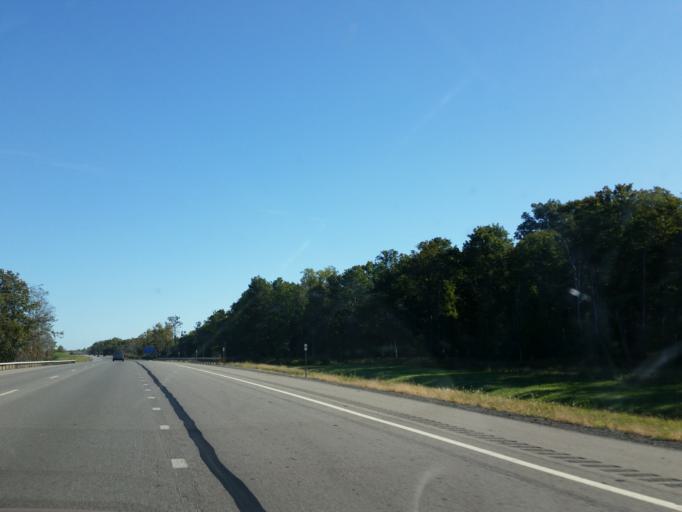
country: US
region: New York
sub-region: Erie County
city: Eden
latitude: 42.6614
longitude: -78.9580
